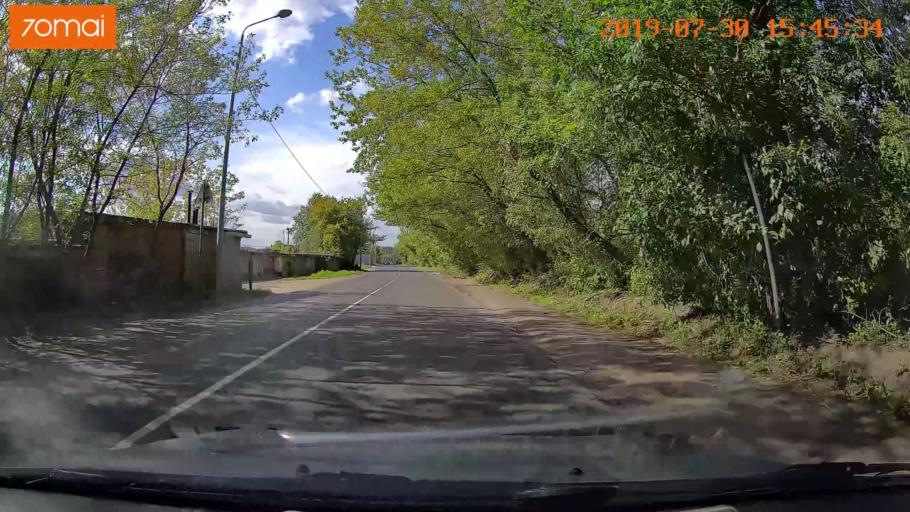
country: RU
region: Moskovskaya
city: Voskresensk
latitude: 55.3276
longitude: 38.6824
